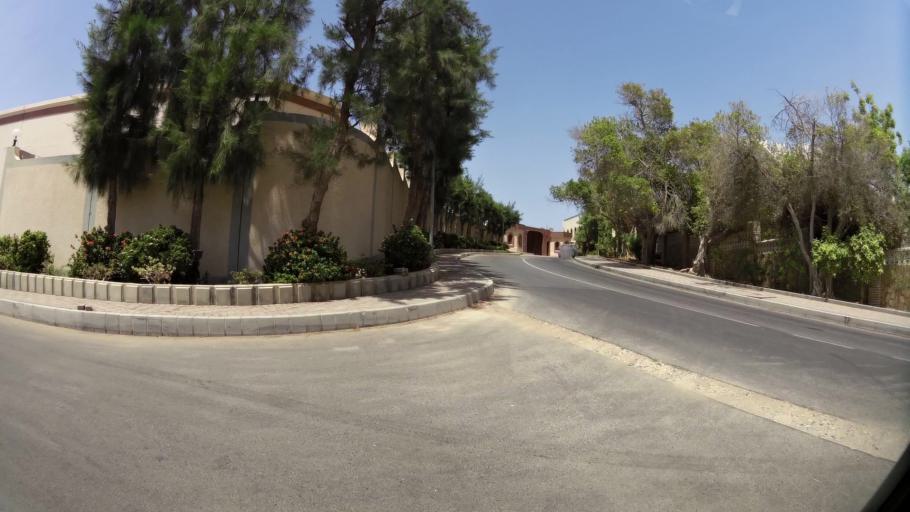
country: OM
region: Muhafazat Masqat
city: Muscat
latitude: 23.6314
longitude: 58.4842
